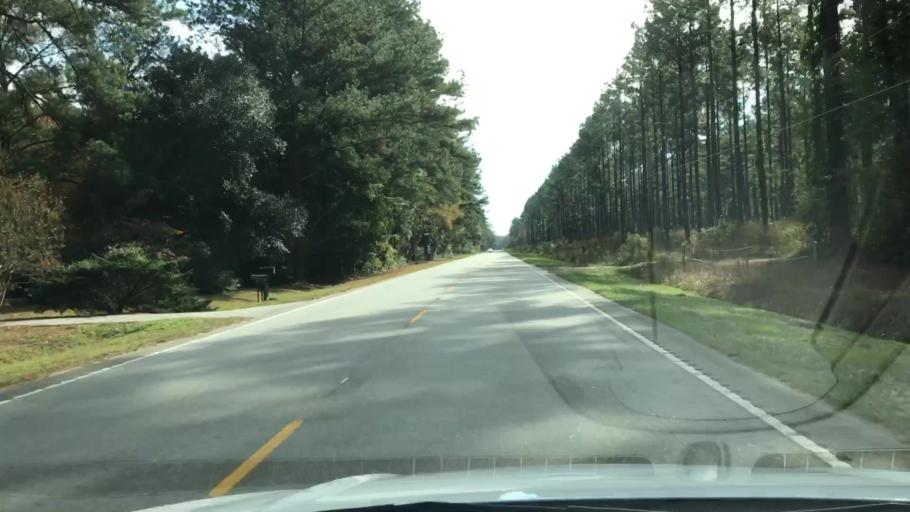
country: US
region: South Carolina
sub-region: Colleton County
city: Walterboro
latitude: 32.7884
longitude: -80.4779
